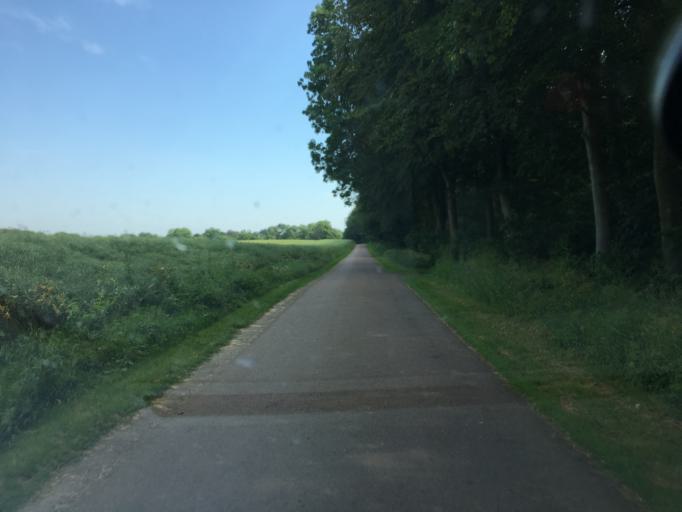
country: DK
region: South Denmark
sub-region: Sonderborg Kommune
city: Dybbol
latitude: 54.9534
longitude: 9.7429
